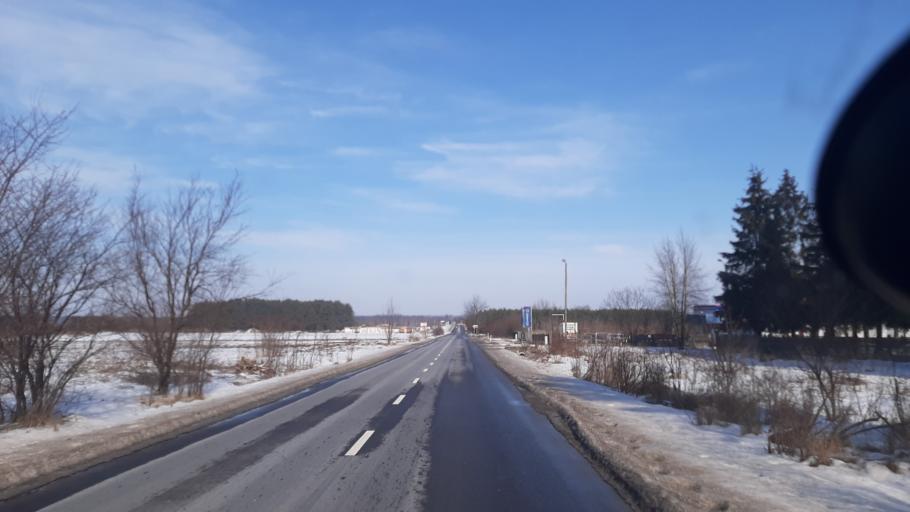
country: PL
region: Lublin Voivodeship
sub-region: Powiat pulawski
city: Kurow
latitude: 51.3987
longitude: 22.1993
